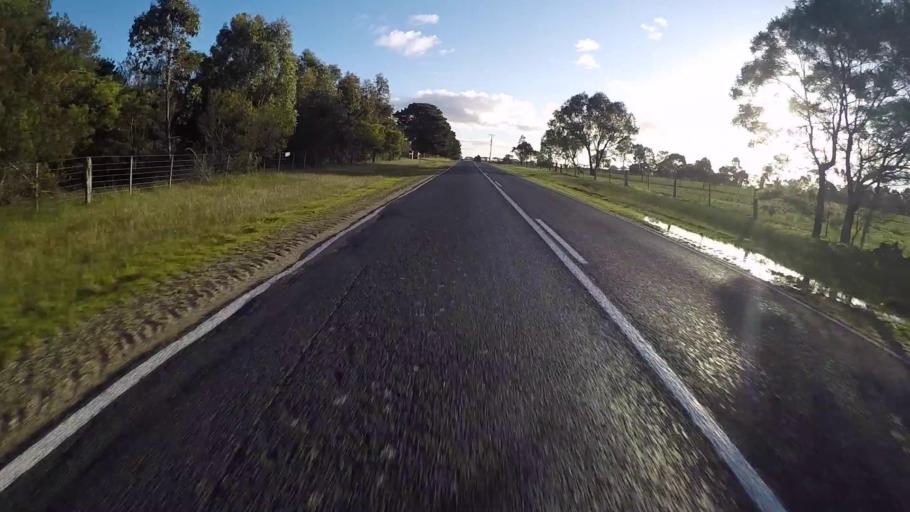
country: AU
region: Victoria
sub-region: Greater Geelong
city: Wandana Heights
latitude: -38.1709
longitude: 144.2056
